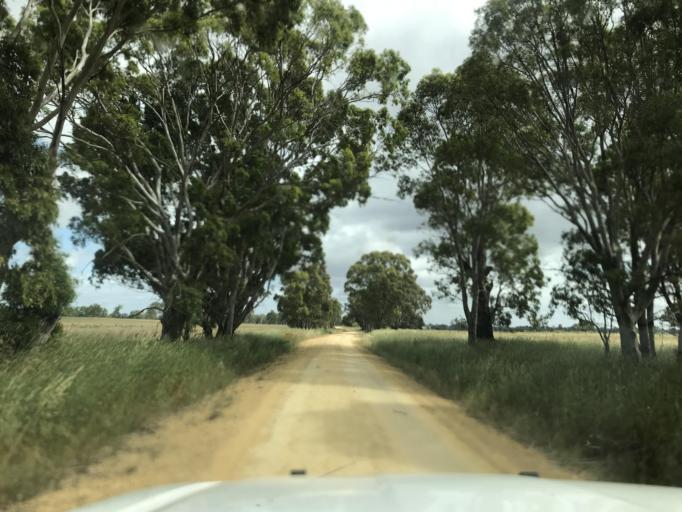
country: AU
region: South Australia
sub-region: Naracoorte and Lucindale
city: Naracoorte
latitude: -36.9244
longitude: 141.4060
